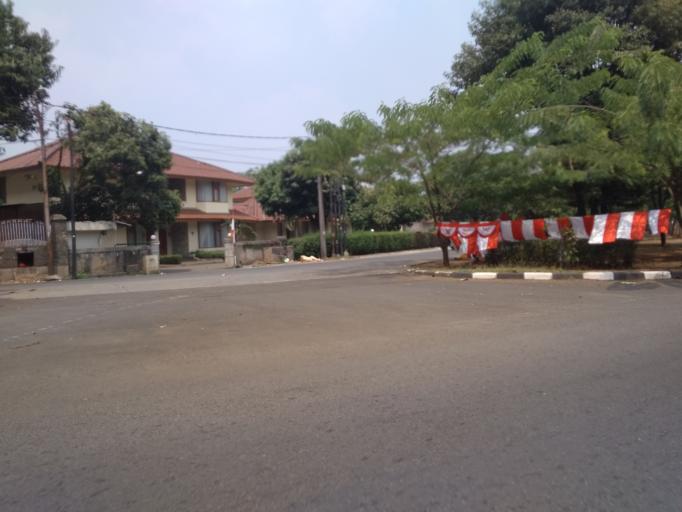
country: ID
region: West Java
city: Pamulang
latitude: -6.3148
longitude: 106.7901
